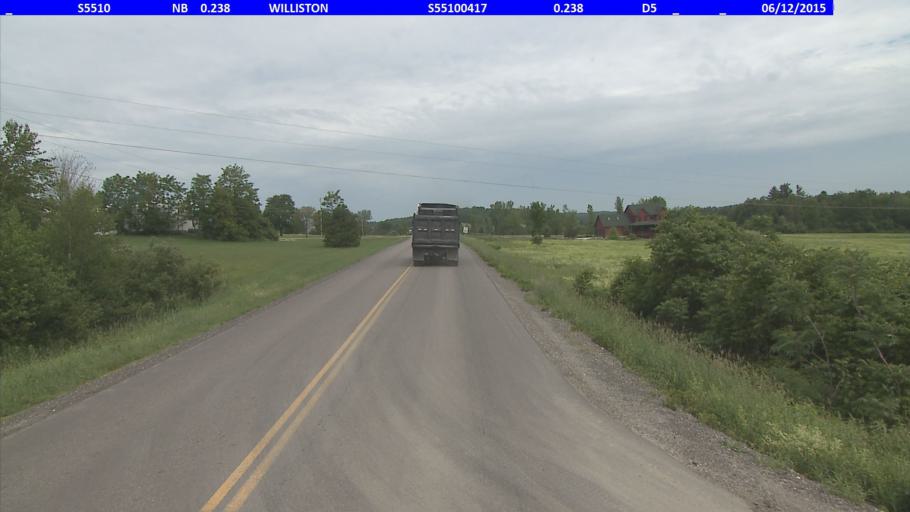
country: US
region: Vermont
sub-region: Chittenden County
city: Hinesburg
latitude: 44.3762
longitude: -73.0944
